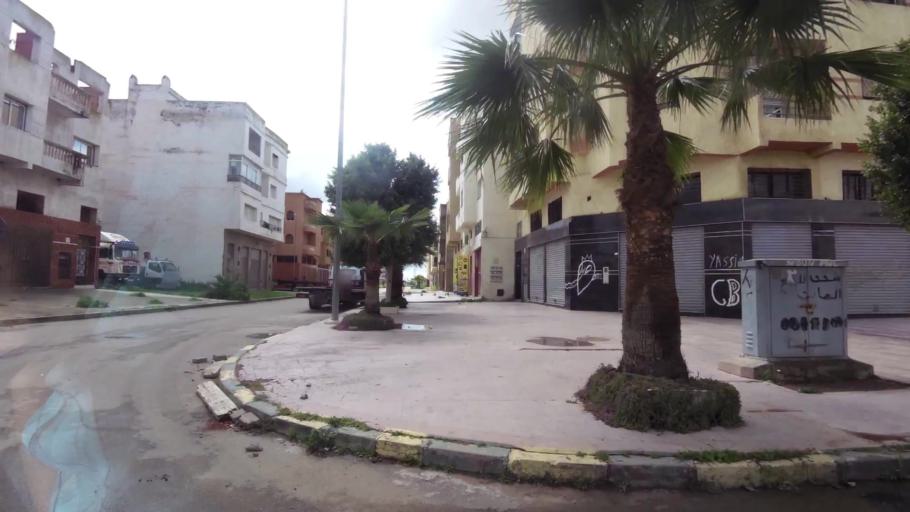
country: MA
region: Chaouia-Ouardigha
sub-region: Settat Province
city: Berrechid
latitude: 33.2618
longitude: -7.5957
